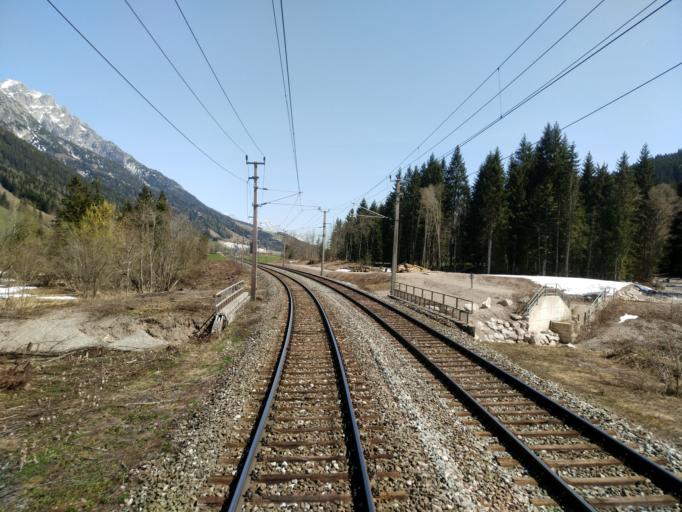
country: AT
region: Tyrol
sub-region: Politischer Bezirk Kitzbuhel
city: Hochfilzen
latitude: 47.4566
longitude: 12.6459
